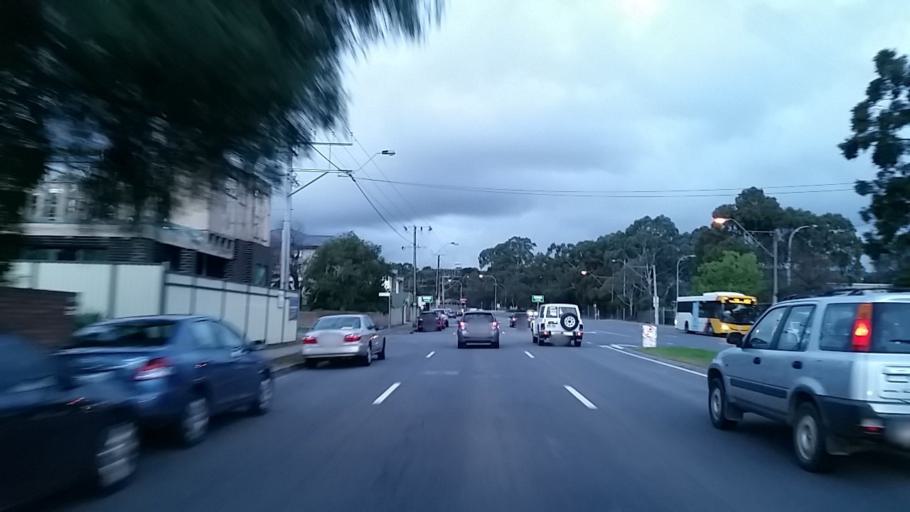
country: AU
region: South Australia
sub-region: Tea Tree Gully
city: Hope Valley
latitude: -34.8272
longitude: 138.7039
